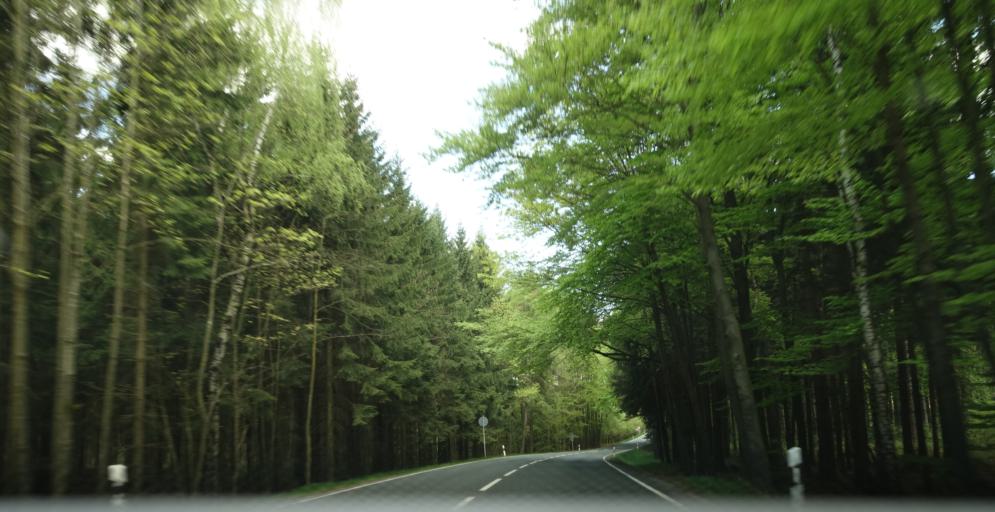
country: DE
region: Saxony
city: Grosshartmannsdorf
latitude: 50.8257
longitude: 13.3261
